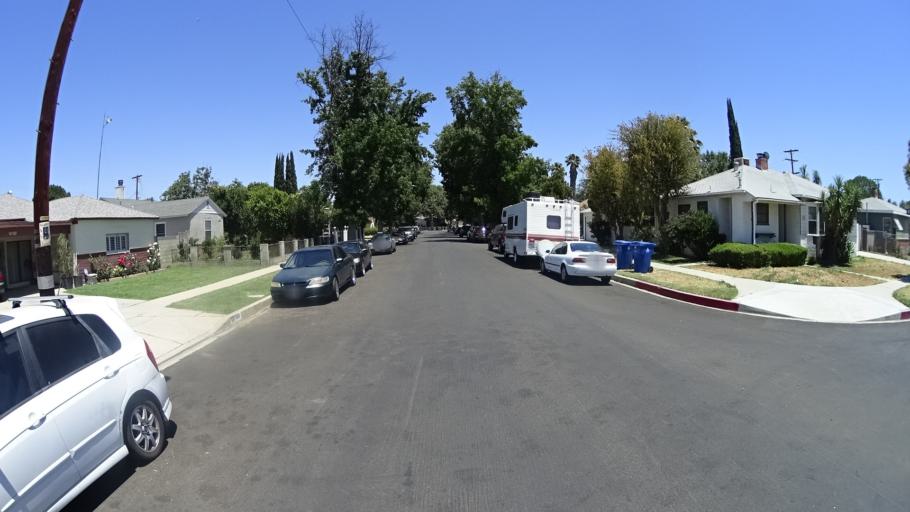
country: US
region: California
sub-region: Los Angeles County
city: Northridge
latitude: 34.1930
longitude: -118.5298
